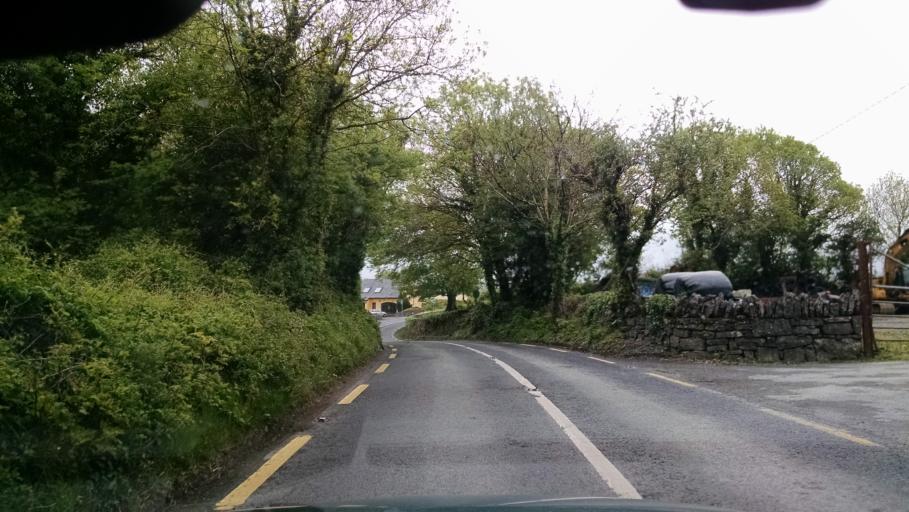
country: IE
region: Connaught
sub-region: County Galway
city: Bearna
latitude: 53.1073
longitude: -9.1556
